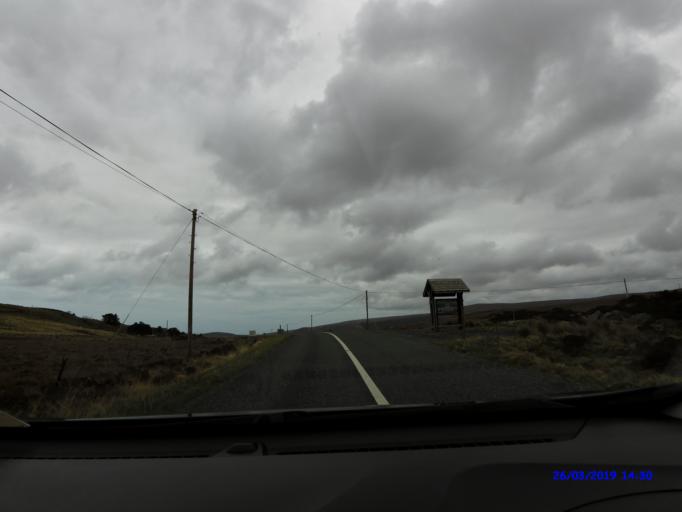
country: IE
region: Connaught
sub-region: Maigh Eo
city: Crossmolina
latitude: 54.2683
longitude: -9.5915
